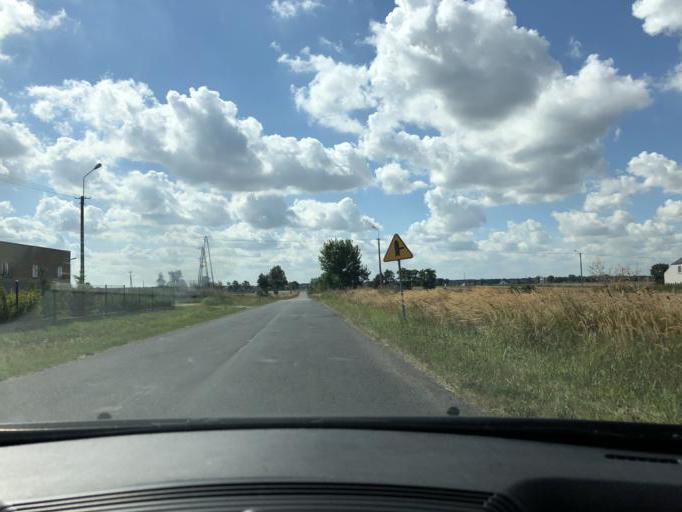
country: PL
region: Lodz Voivodeship
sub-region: Powiat wieruszowski
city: Walichnowy
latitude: 51.2474
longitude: 18.3892
